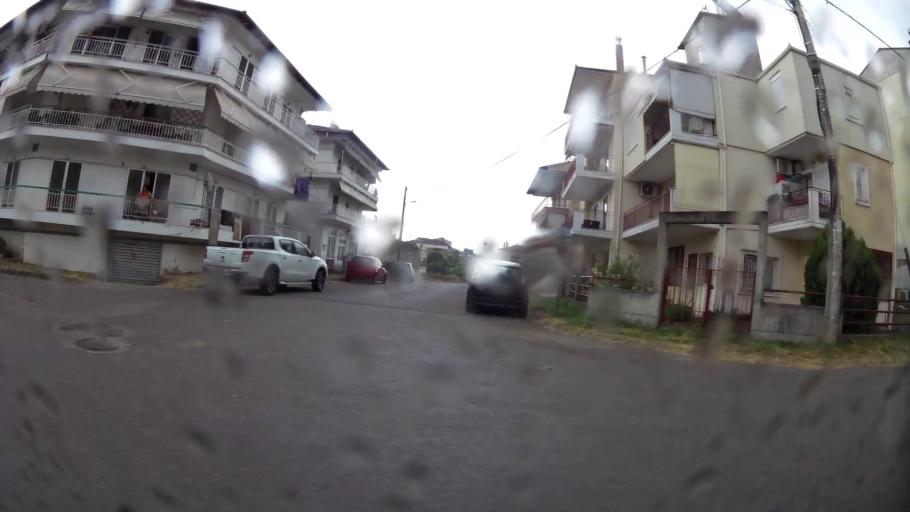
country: GR
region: Central Macedonia
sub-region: Nomos Imathias
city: Veroia
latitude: 40.5260
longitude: 22.1962
